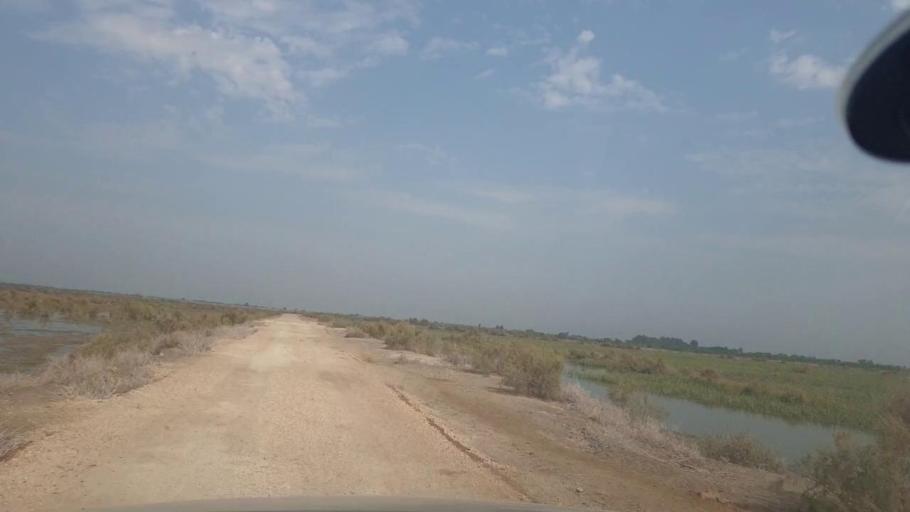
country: PK
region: Balochistan
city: Mehrabpur
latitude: 28.0413
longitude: 68.1234
